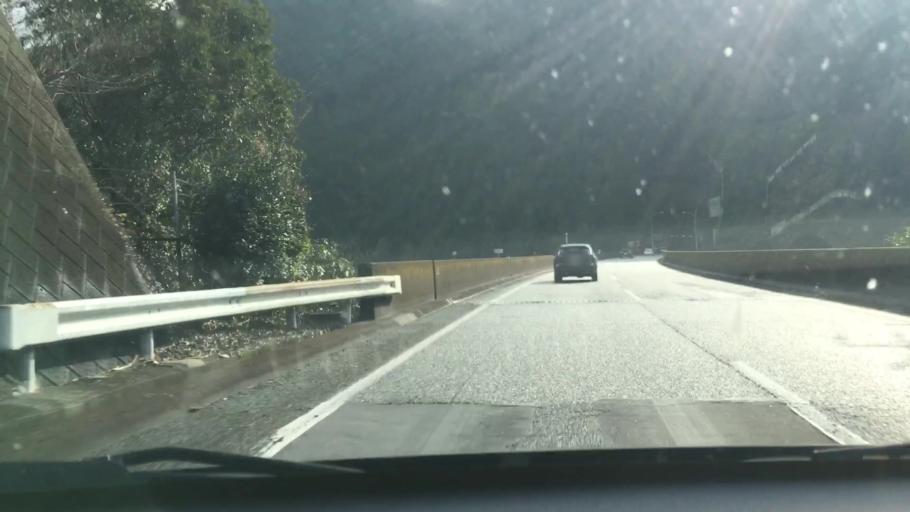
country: JP
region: Kumamoto
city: Yatsushiro
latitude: 32.4261
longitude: 130.7024
